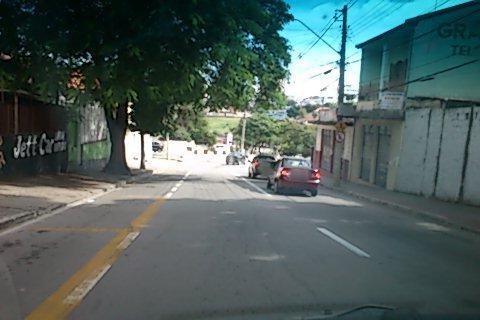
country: BR
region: Sao Paulo
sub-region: Sao Jose Dos Campos
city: Sao Jose dos Campos
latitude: -23.1886
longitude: -45.8781
